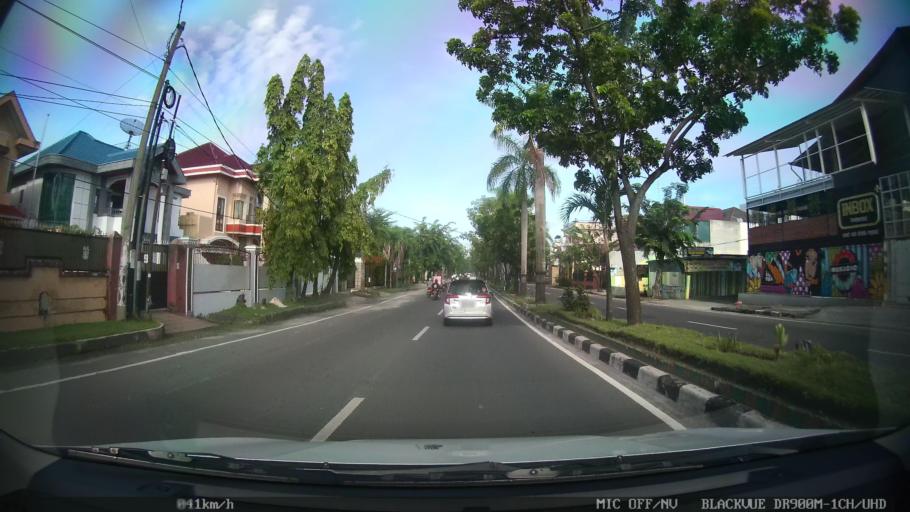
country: ID
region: North Sumatra
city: Medan
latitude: 3.6078
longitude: 98.6573
